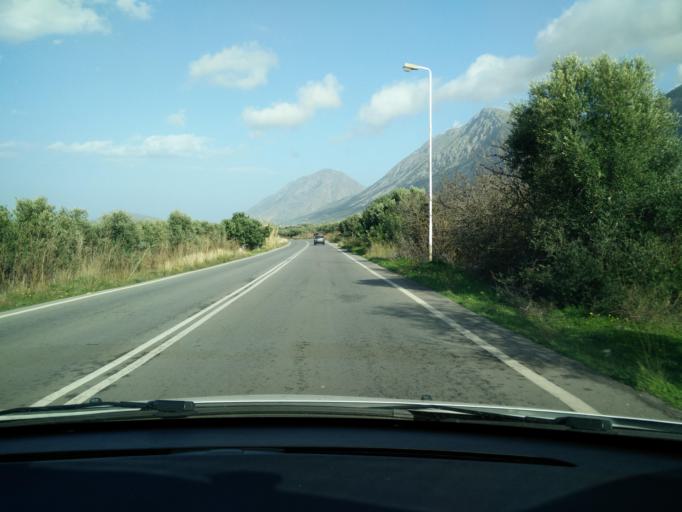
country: GR
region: Crete
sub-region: Nomos Lasithiou
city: Kato Chorio
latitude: 35.0706
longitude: 25.8042
